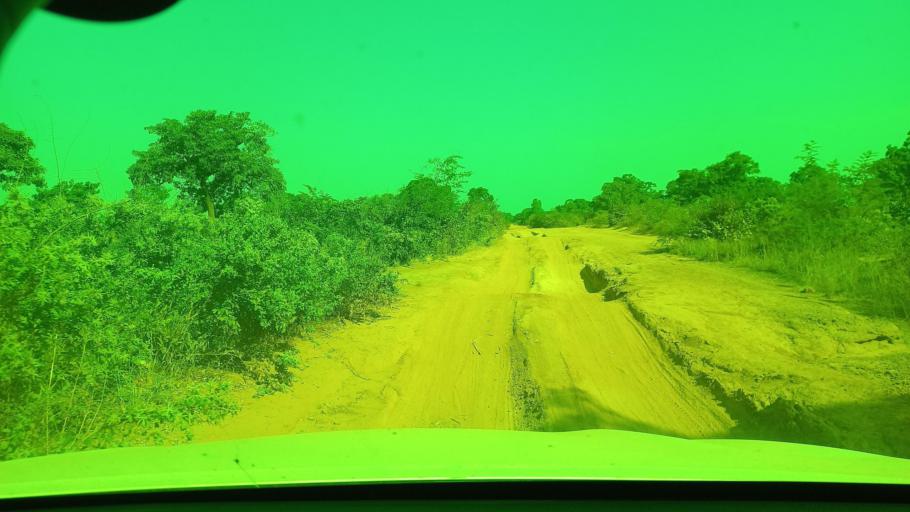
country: ML
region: Bamako
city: Bamako
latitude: 12.3963
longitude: -7.9782
